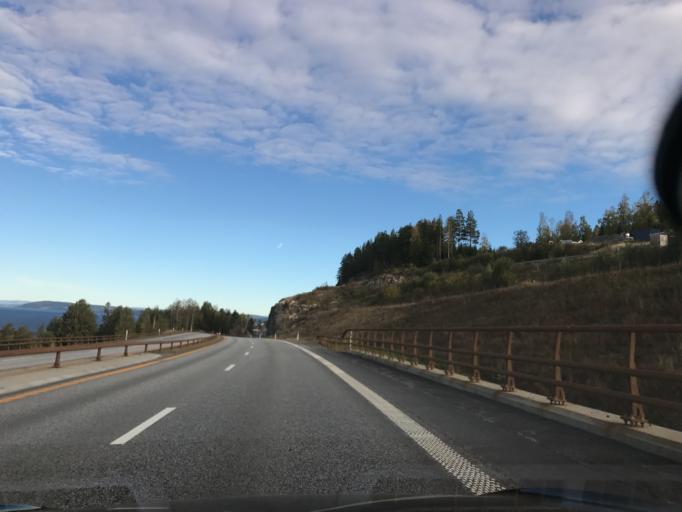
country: NO
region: Akershus
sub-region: Eidsvoll
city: Eidsvoll
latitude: 60.4991
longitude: 11.2385
